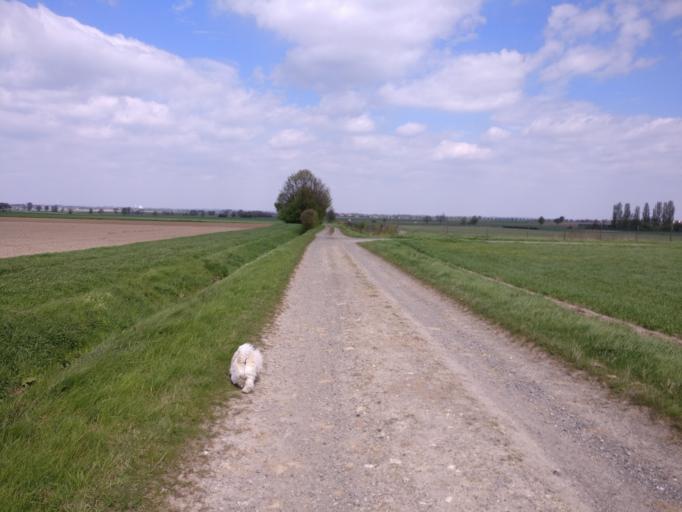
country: DE
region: Lower Saxony
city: Schellerten
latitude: 52.1373
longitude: 10.0573
